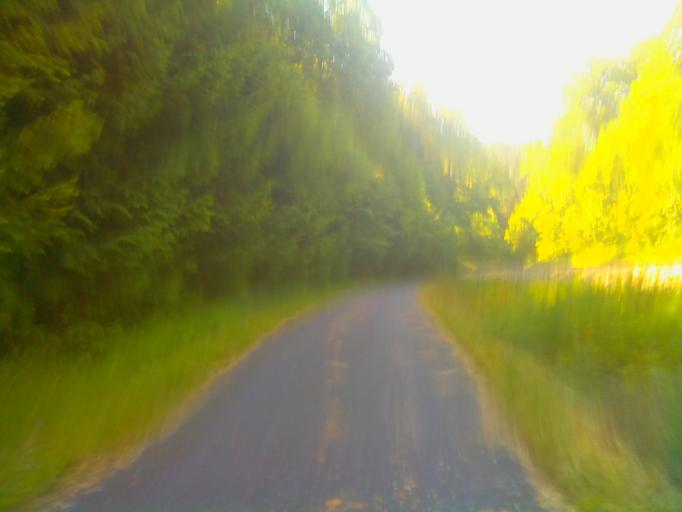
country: DE
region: Thuringia
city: Freienorla
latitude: 50.7547
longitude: 11.5461
